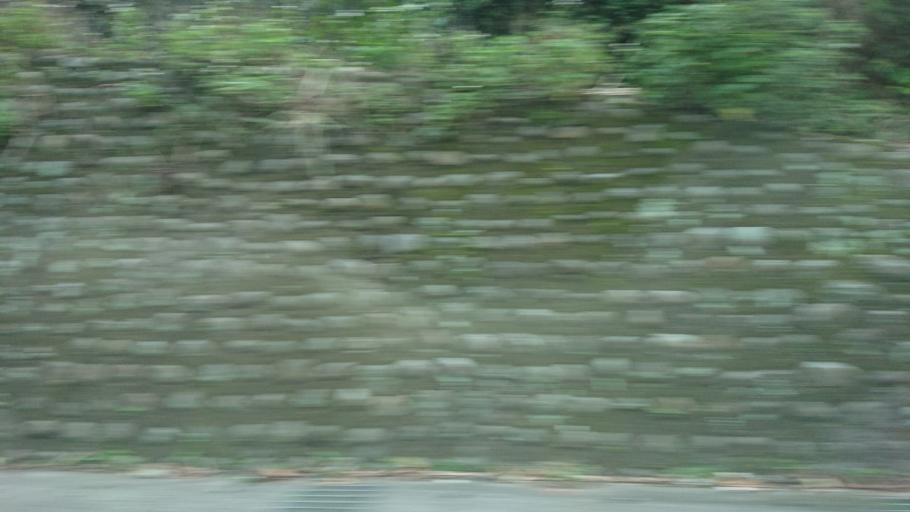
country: TW
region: Taiwan
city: Daxi
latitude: 24.8764
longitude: 121.3819
